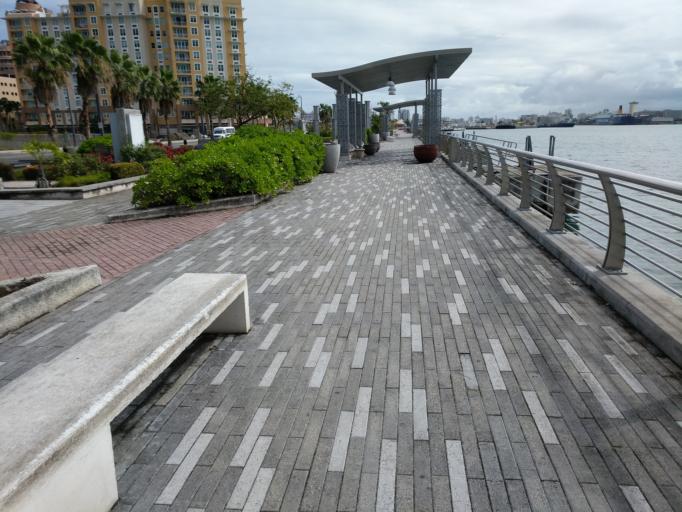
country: PR
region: San Juan
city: San Juan
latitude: 18.4636
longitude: -66.1092
